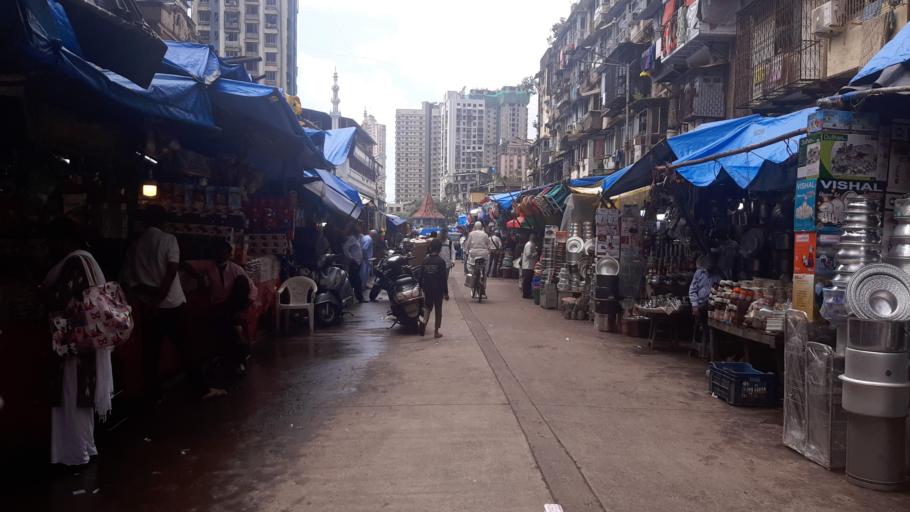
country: IN
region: Maharashtra
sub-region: Mumbai Suburban
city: Mumbai
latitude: 18.9579
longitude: 72.8310
